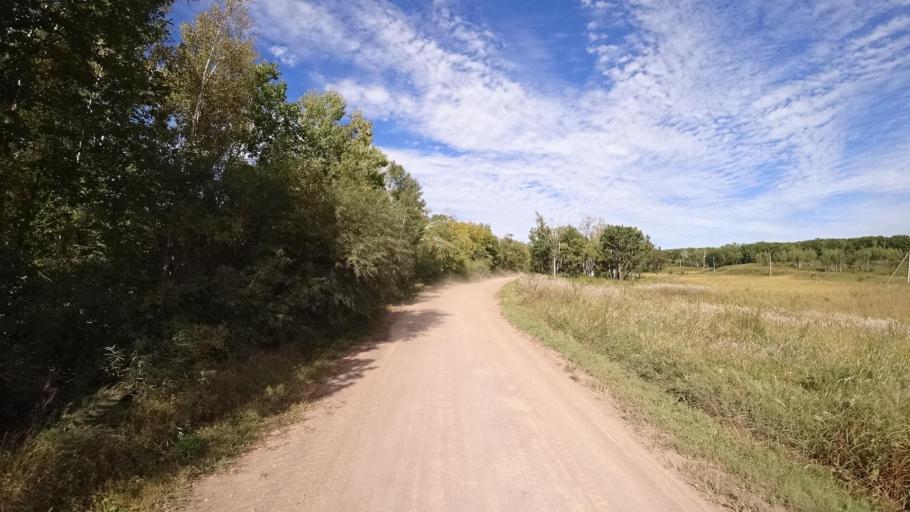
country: RU
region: Primorskiy
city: Yakovlevka
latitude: 44.3899
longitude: 133.5472
